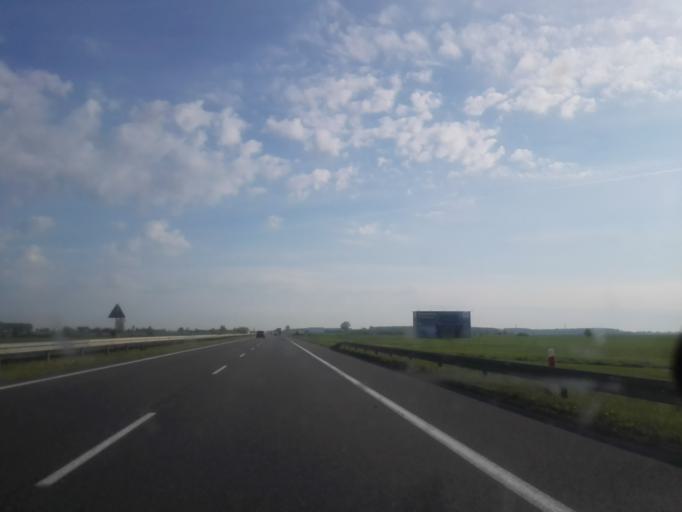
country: PL
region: Lodz Voivodeship
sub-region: Powiat piotrkowski
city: Wola Krzysztoporska
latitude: 51.3658
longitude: 19.6143
